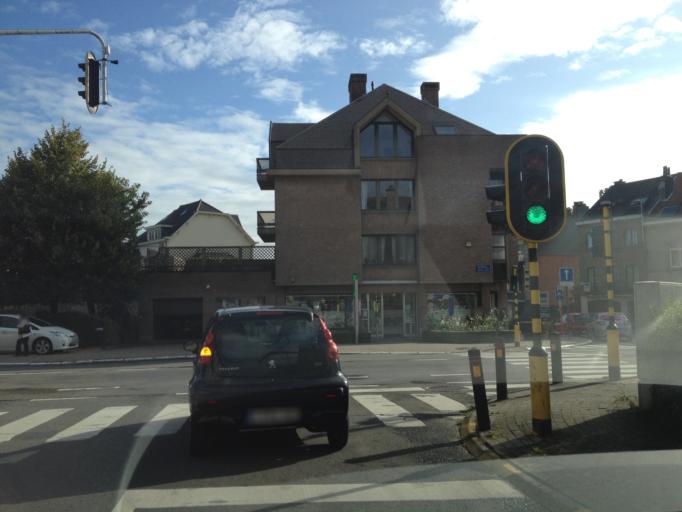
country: BE
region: Flanders
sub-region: Provincie Vlaams-Brabant
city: Wemmel
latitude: 50.9042
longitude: 4.3040
